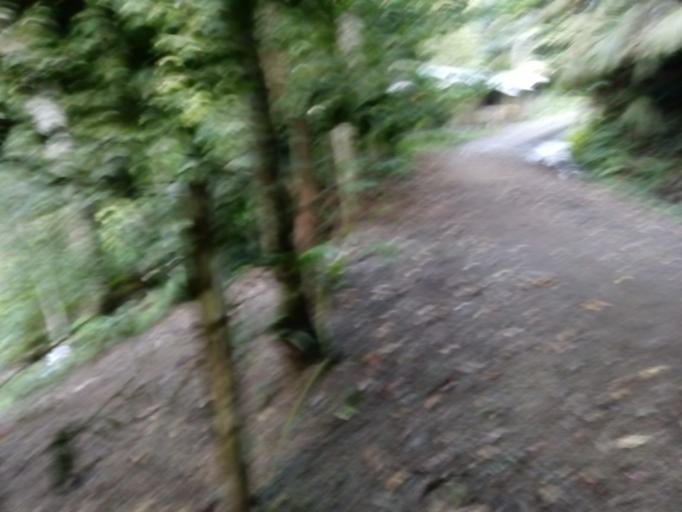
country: CO
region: Boyaca
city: Otanche
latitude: 5.8554
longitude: -74.3272
